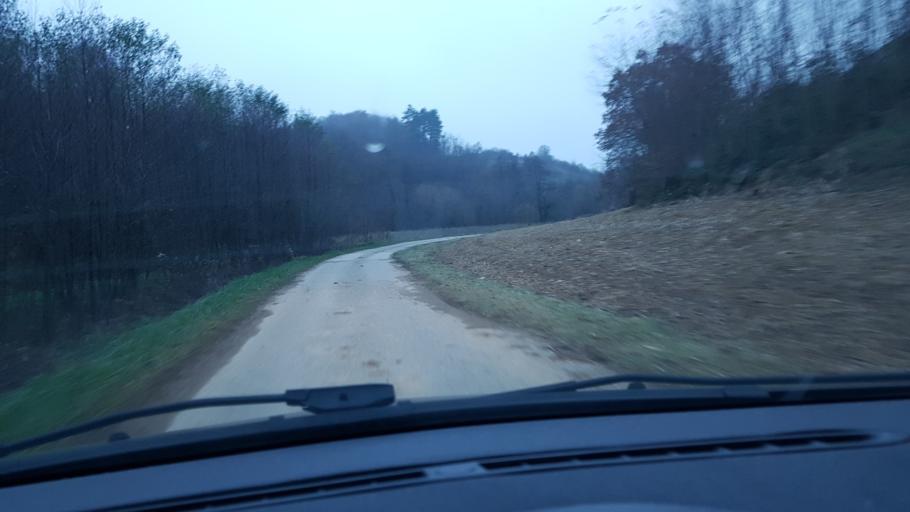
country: HR
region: Krapinsko-Zagorska
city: Pregrada
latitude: 46.2078
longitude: 15.7946
